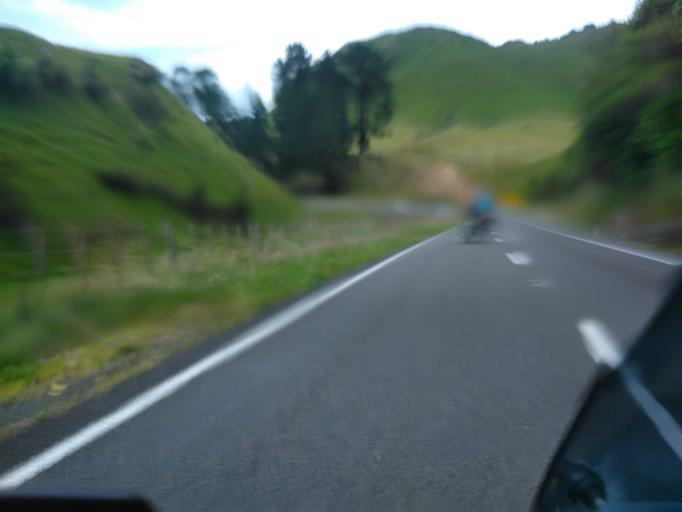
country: NZ
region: Bay of Plenty
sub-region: Opotiki District
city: Opotiki
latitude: -38.3728
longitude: 177.4648
